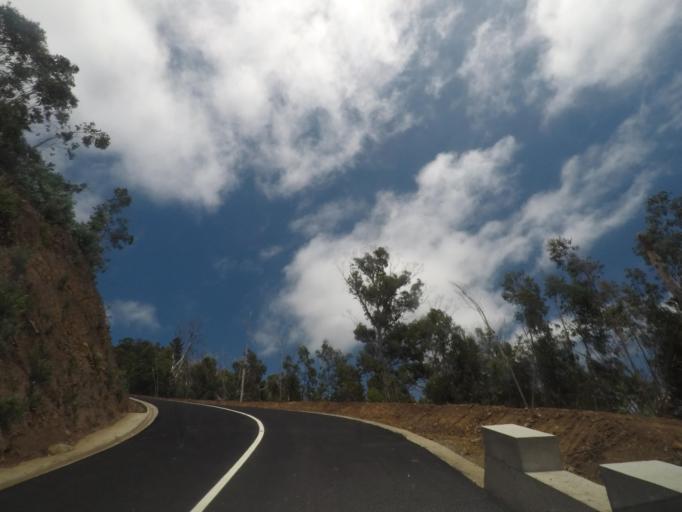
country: PT
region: Madeira
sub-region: Calheta
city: Estreito da Calheta
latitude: 32.7431
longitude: -17.1593
